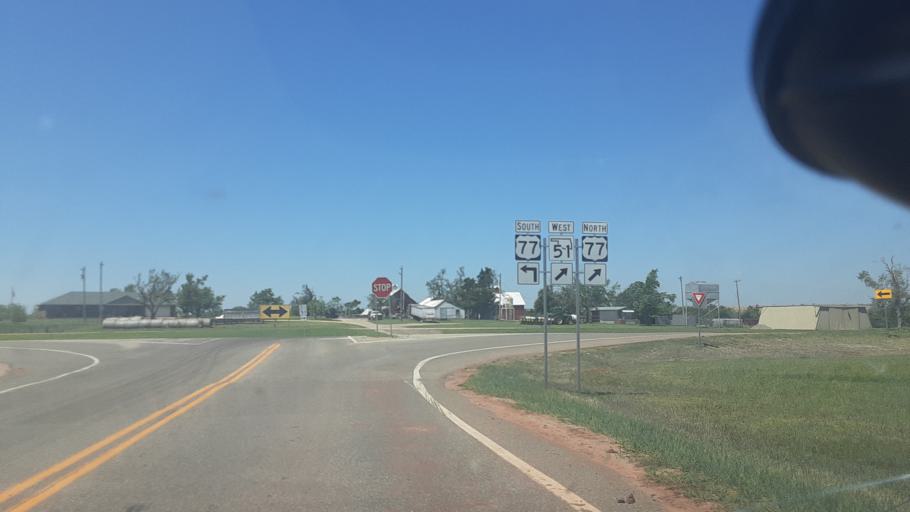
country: US
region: Oklahoma
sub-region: Noble County
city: Perry
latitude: 36.1111
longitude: -97.3881
